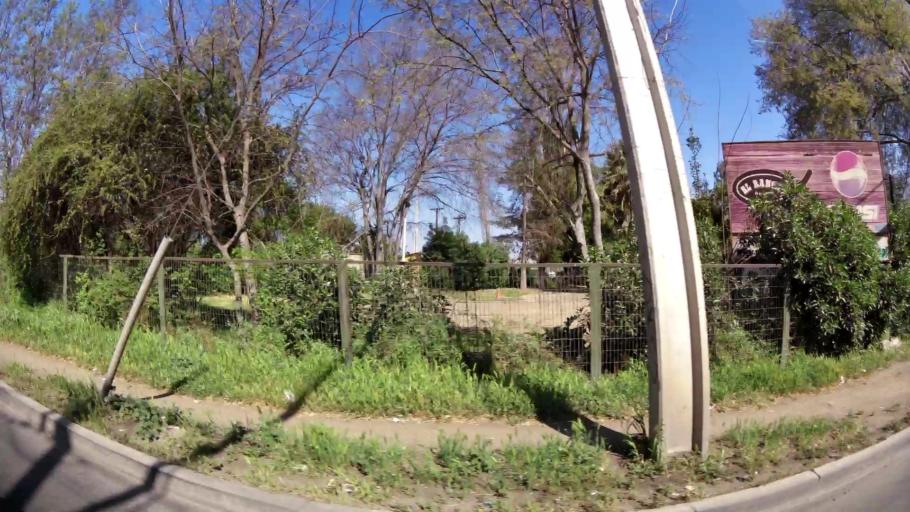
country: CL
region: Santiago Metropolitan
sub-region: Provincia de Chacabuco
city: Chicureo Abajo
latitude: -33.3674
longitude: -70.6736
